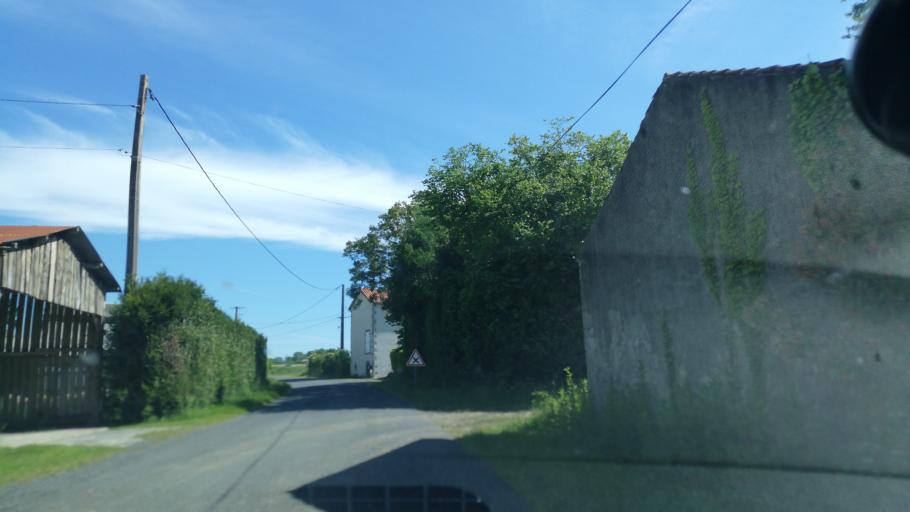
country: FR
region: Poitou-Charentes
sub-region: Departement des Deux-Sevres
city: Moncoutant
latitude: 46.6868
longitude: -0.5730
